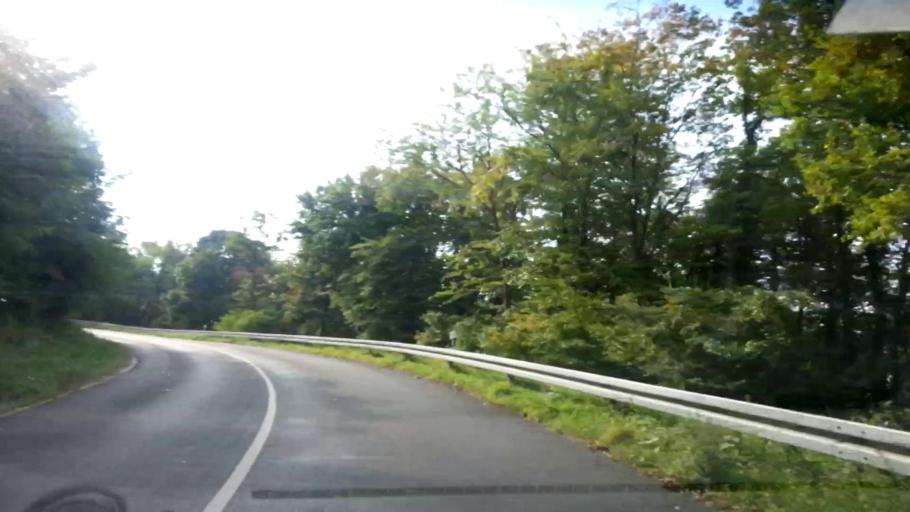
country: DE
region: Bavaria
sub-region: Regierungsbezirk Unterfranken
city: Rodelsee
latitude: 49.7273
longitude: 10.2689
